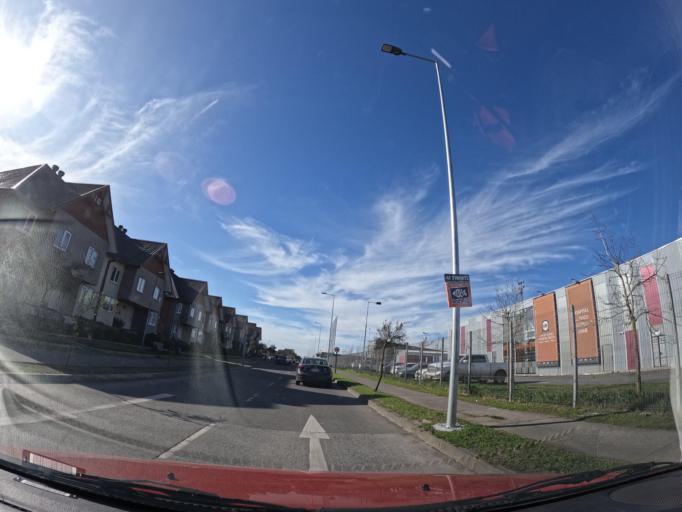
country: CL
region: Biobio
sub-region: Provincia de Concepcion
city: Concepcion
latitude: -36.7730
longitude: -73.0672
